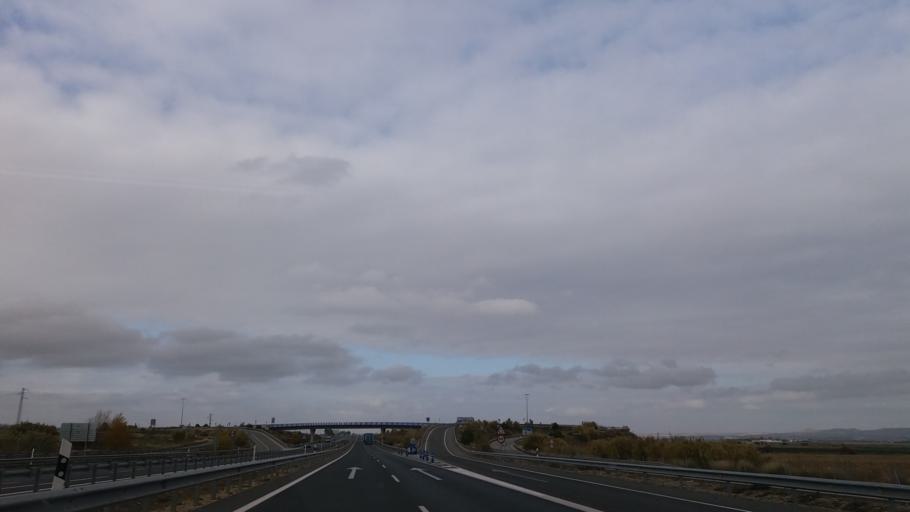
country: ES
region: Navarre
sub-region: Provincia de Navarra
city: Cortes
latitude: 41.9284
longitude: -1.4542
